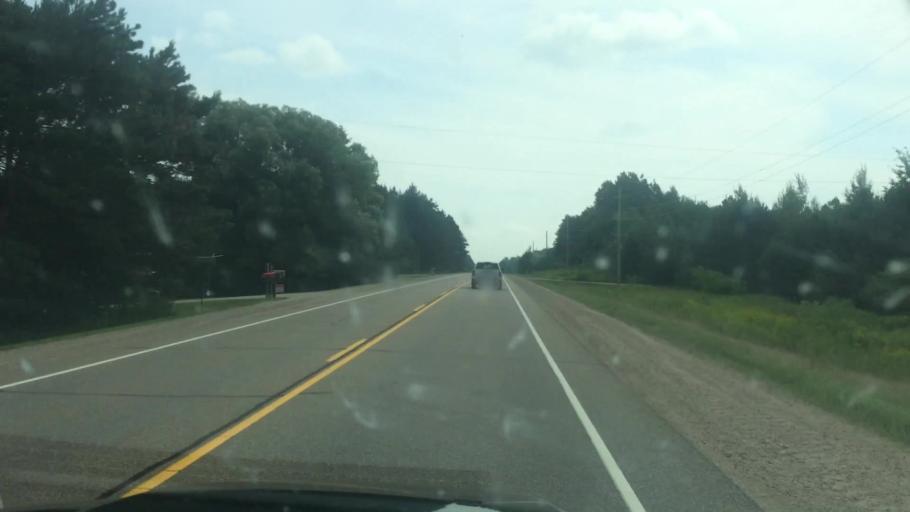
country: US
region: Wisconsin
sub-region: Langlade County
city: Antigo
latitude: 45.1617
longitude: -89.0590
